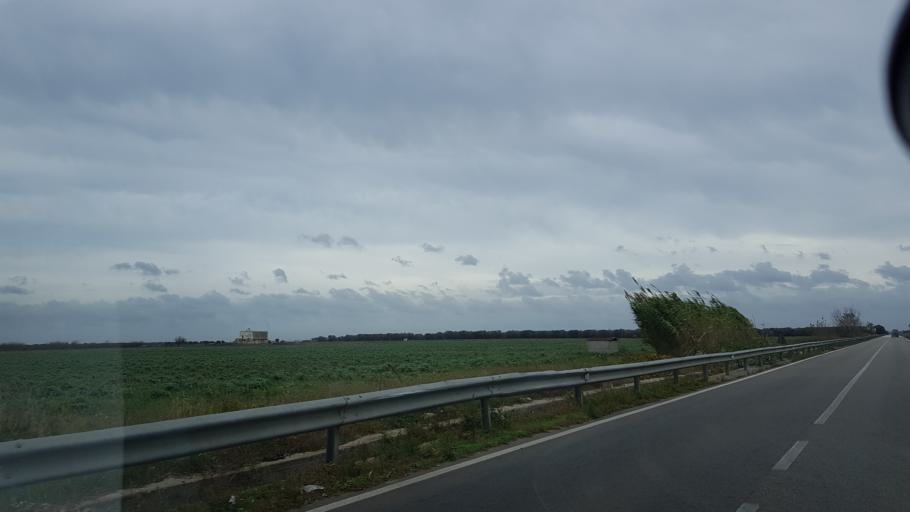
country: IT
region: Apulia
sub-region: Provincia di Brindisi
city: San Pancrazio Salentino
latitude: 40.4100
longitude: 17.8732
